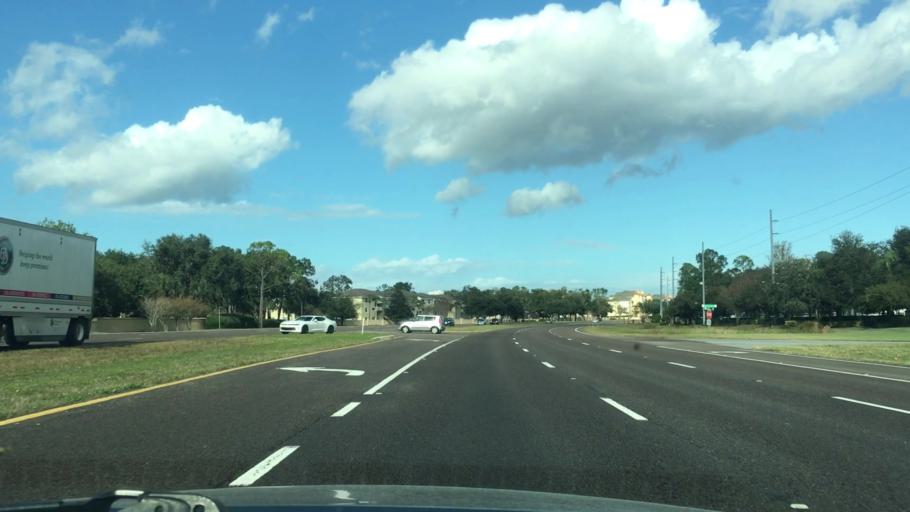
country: US
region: Florida
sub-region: Osceola County
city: Celebration
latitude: 28.3608
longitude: -81.4999
